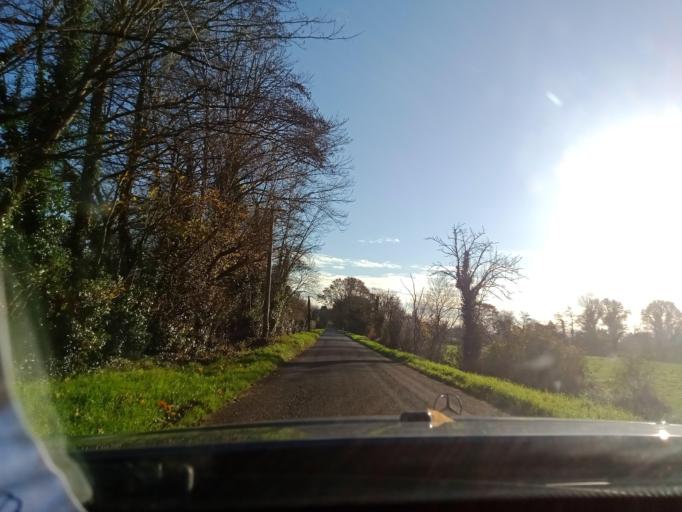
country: IE
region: Leinster
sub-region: Kilkenny
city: Piltown
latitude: 52.3480
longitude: -7.2801
